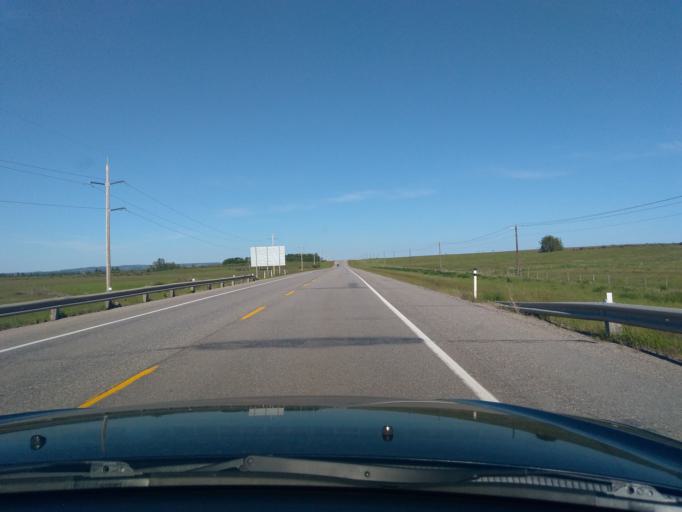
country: CA
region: Alberta
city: Cochrane
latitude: 51.0234
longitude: -114.4550
